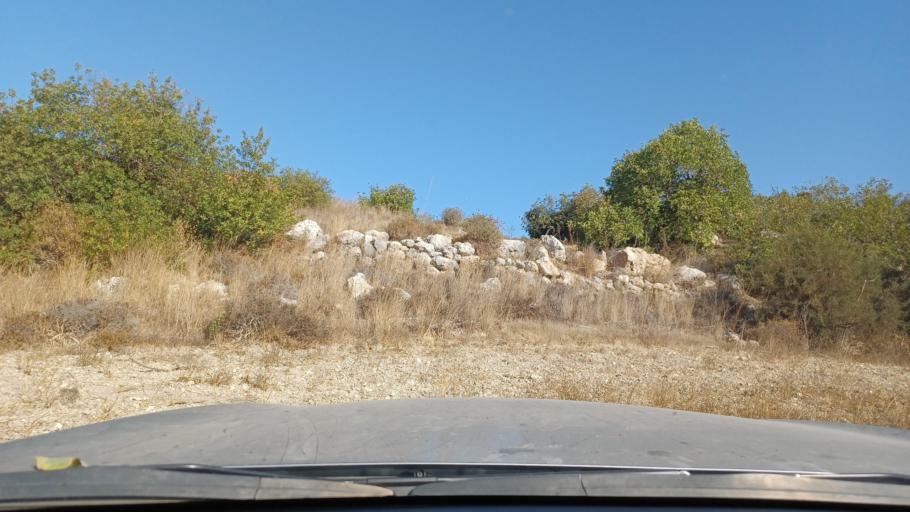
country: CY
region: Pafos
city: Polis
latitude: 35.0029
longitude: 32.4906
